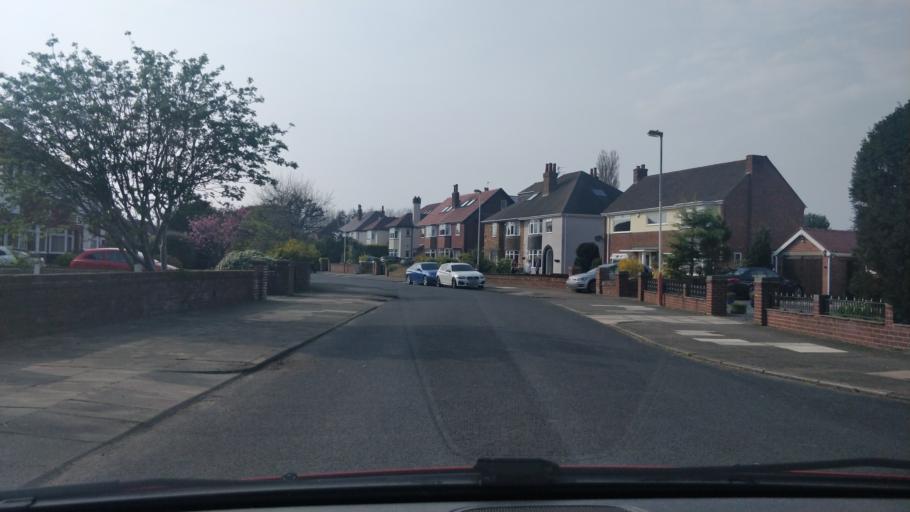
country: GB
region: England
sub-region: Sefton
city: Formby
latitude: 53.5991
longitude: -3.0411
